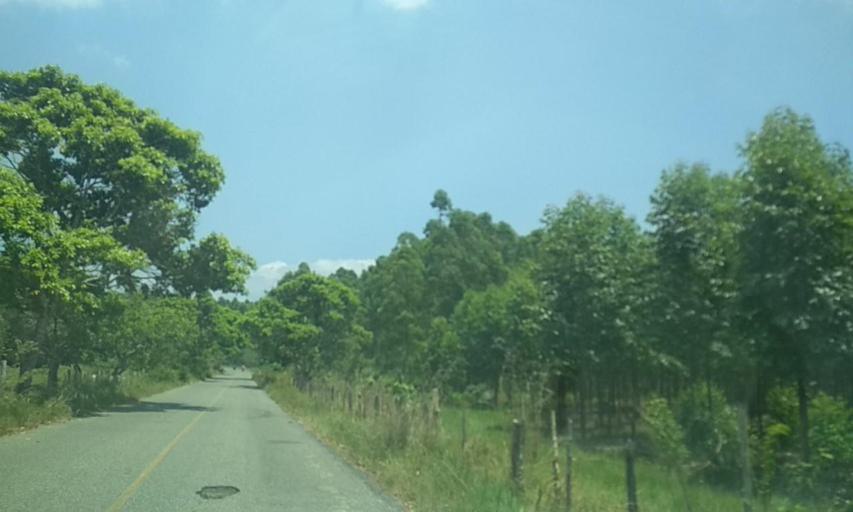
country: MX
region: Tabasco
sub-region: Huimanguillo
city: Francisco Rueda
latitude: 17.8381
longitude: -93.9068
